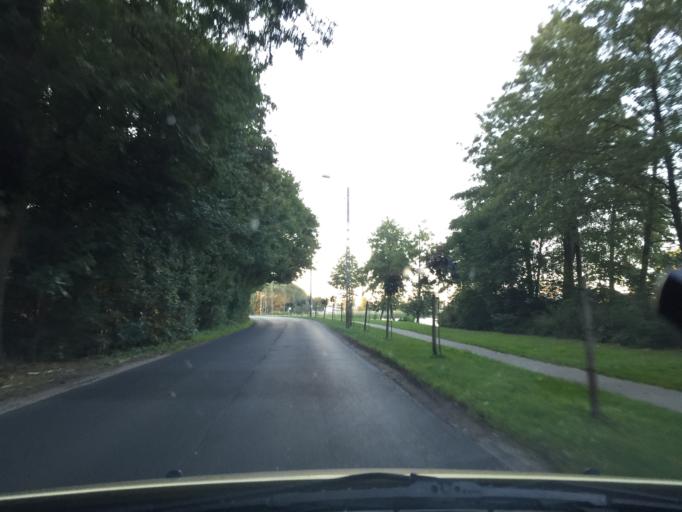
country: PL
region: Greater Poland Voivodeship
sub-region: Powiat pleszewski
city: Dobrzyca
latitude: 51.8650
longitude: 17.6089
